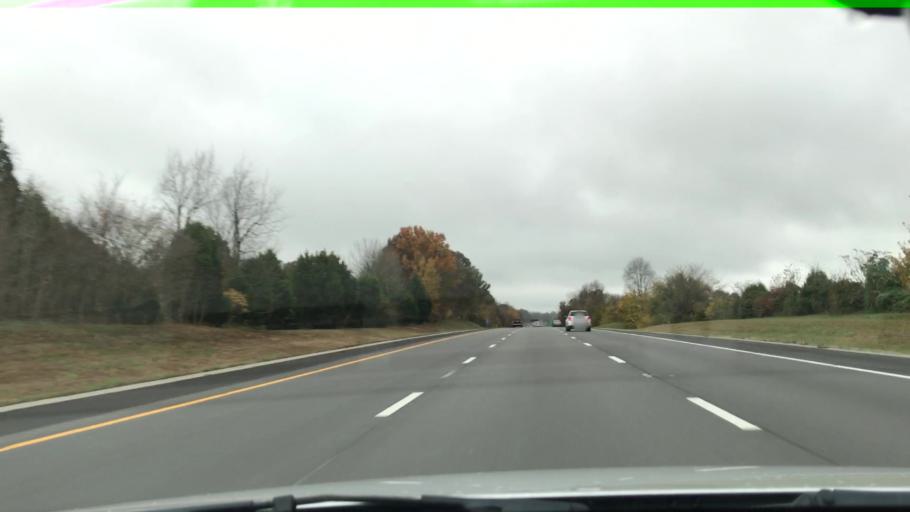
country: US
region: Kentucky
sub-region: Warren County
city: Bowling Green
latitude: 37.0172
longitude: -86.2752
